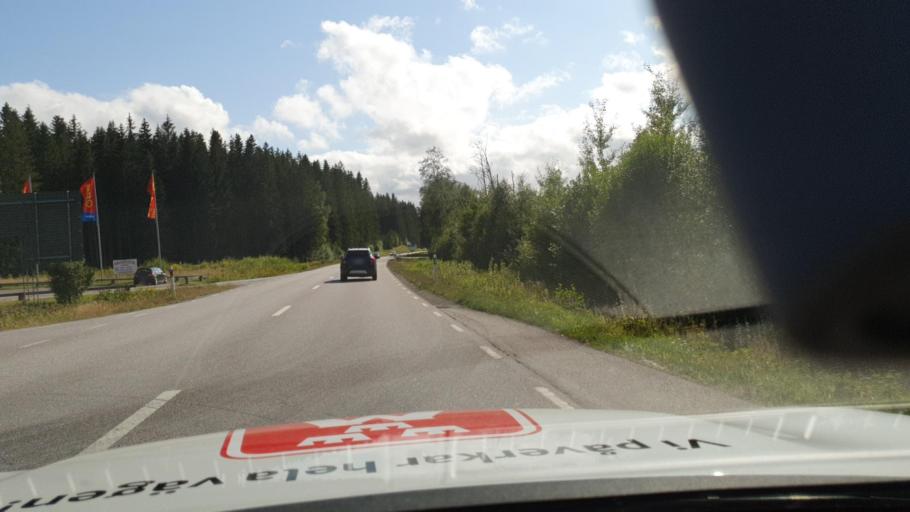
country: SE
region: Vaestra Goetaland
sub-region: Bengtsfors Kommun
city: Billingsfors
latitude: 58.9561
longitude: 12.2298
